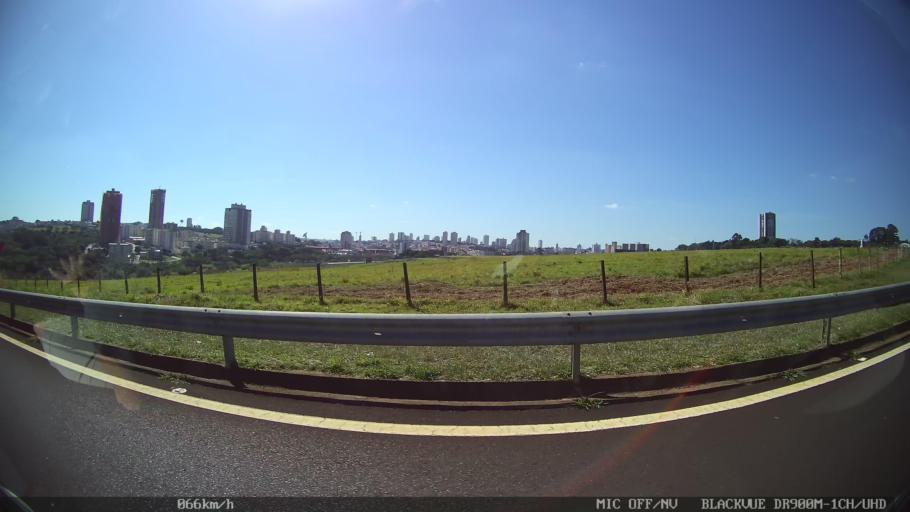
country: BR
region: Sao Paulo
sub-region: Franca
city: Franca
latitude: -20.5603
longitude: -47.4143
